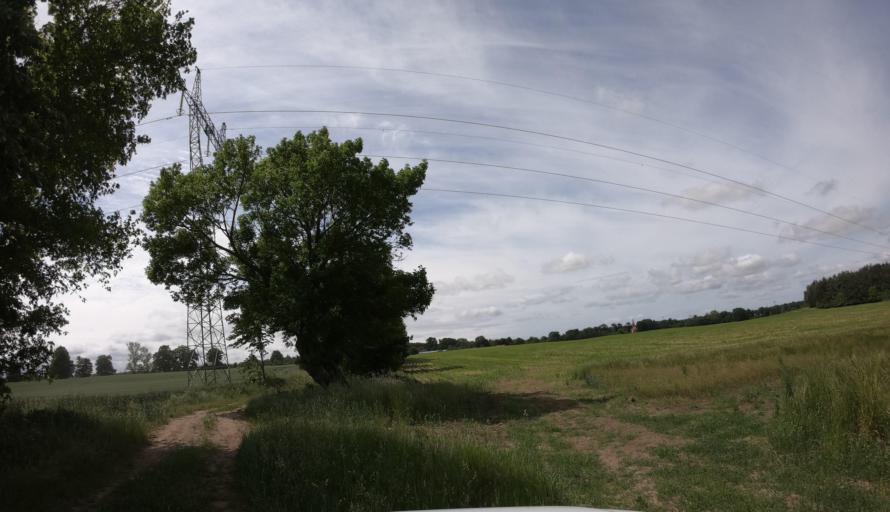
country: PL
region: West Pomeranian Voivodeship
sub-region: Powiat goleniowski
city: Przybiernow
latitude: 53.8264
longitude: 14.7195
